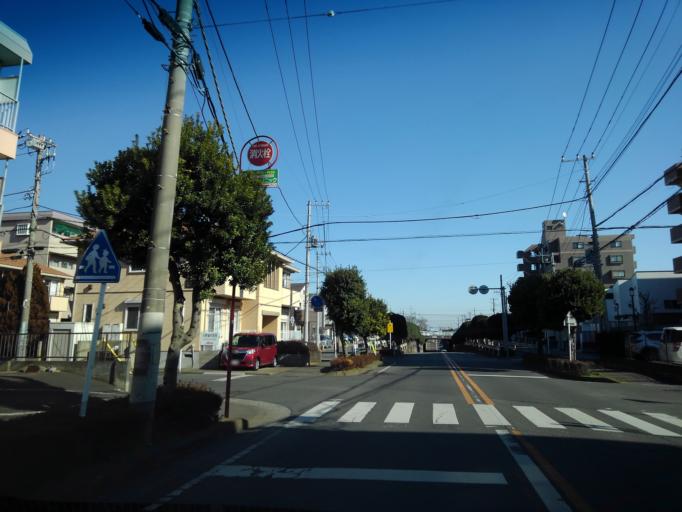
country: JP
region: Saitama
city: Tokorozawa
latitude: 35.7994
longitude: 139.5192
